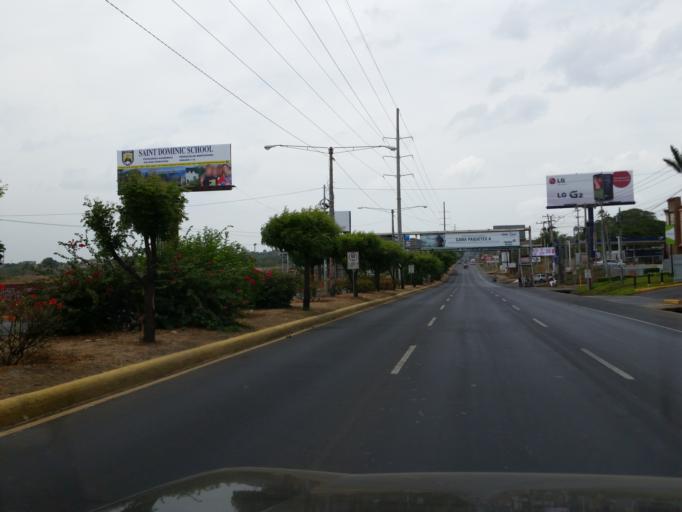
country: NI
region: Managua
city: Managua
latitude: 12.1054
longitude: -86.2482
